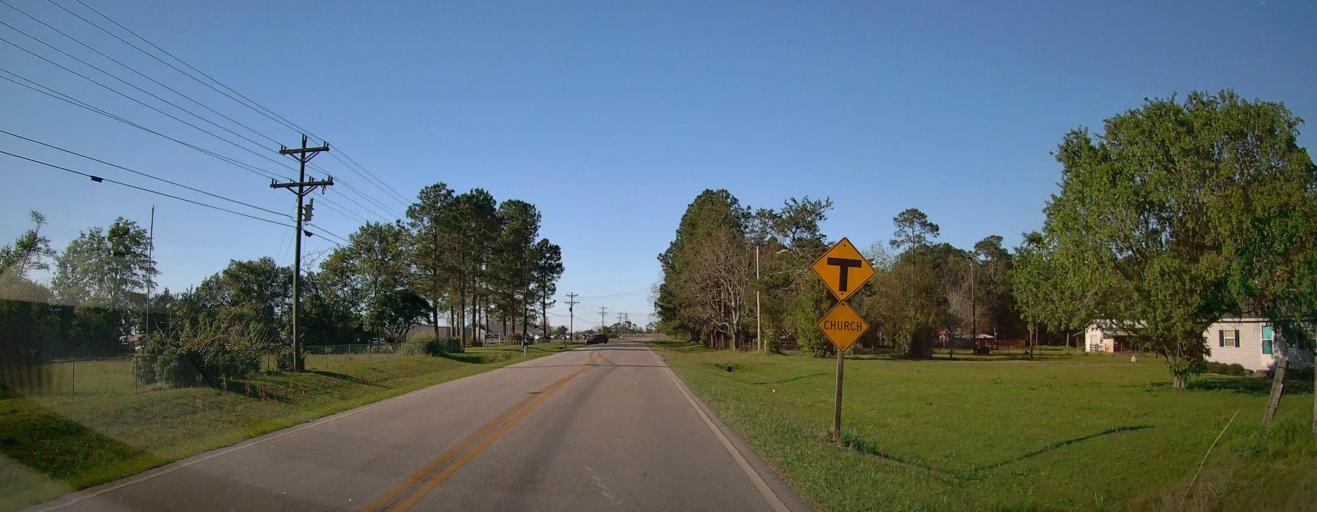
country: US
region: Georgia
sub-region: Ben Hill County
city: Fitzgerald
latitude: 31.7399
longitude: -83.2347
